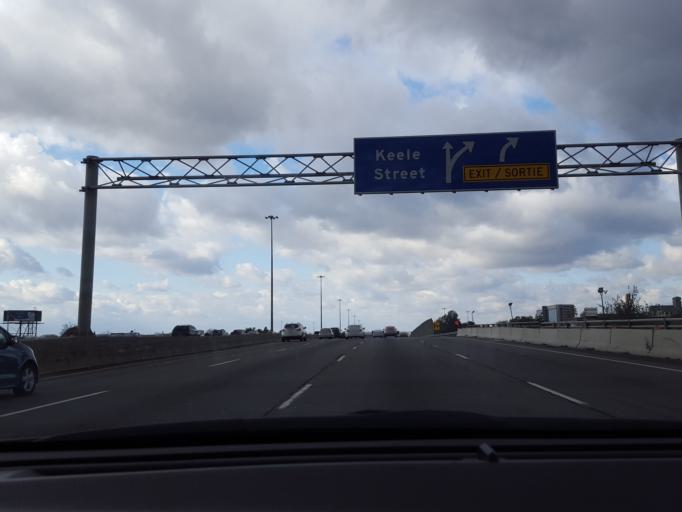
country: CA
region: Ontario
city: Toronto
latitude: 43.7253
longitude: -79.4716
